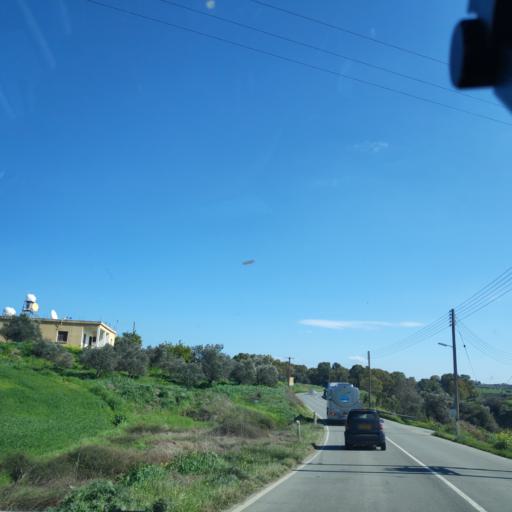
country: CY
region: Lefkosia
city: Alampra
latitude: 35.0116
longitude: 33.3449
